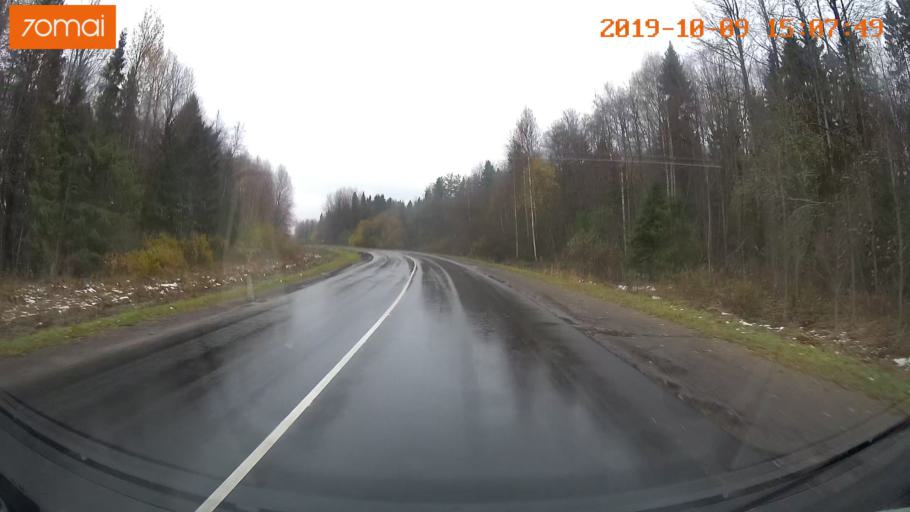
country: RU
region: Kostroma
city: Susanino
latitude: 58.2144
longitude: 41.6466
